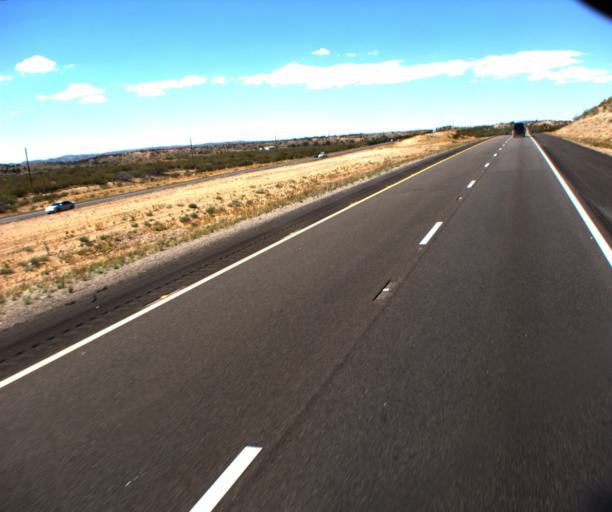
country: US
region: Arizona
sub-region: Mohave County
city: Kingman
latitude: 35.0185
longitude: -113.6640
